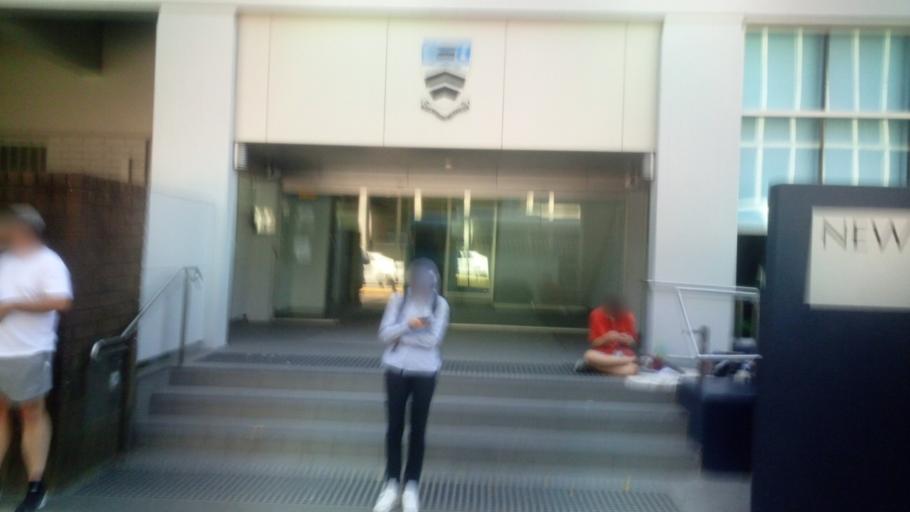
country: AU
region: New South Wales
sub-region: Randwick
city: Kensington
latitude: -33.9183
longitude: 151.2264
